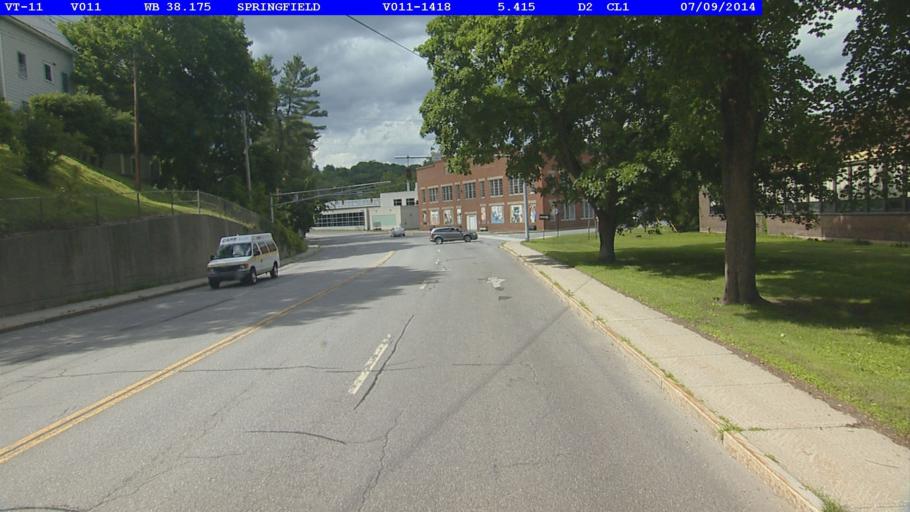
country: US
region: Vermont
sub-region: Windsor County
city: Springfield
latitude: 43.2903
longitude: -72.4728
